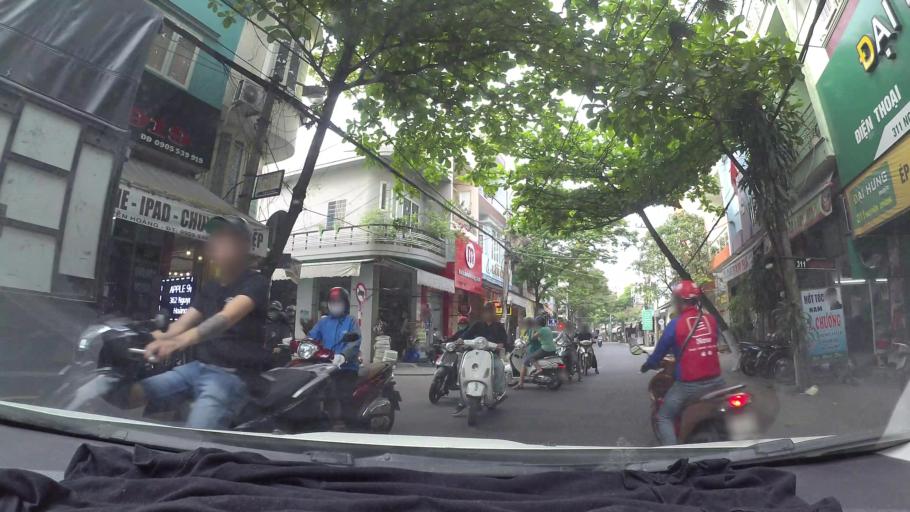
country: VN
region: Da Nang
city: Da Nang
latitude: 16.0559
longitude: 108.2128
